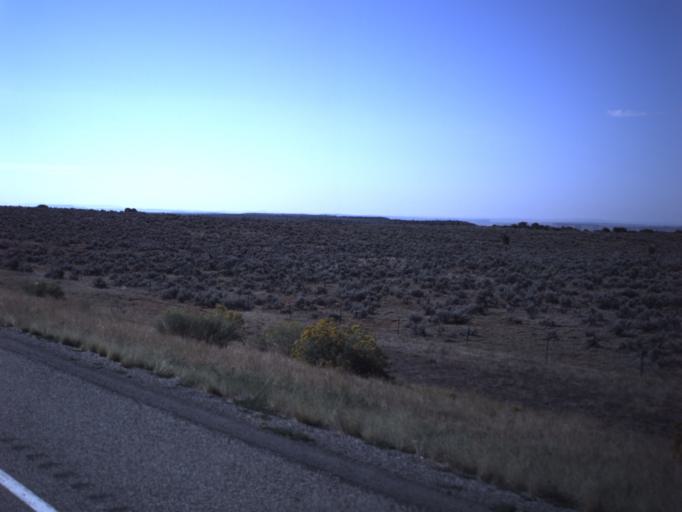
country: US
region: Utah
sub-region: San Juan County
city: Blanding
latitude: 37.5033
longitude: -109.4873
